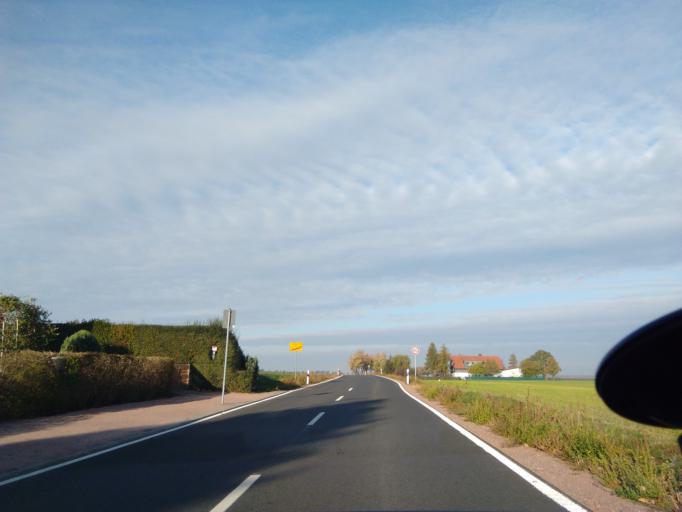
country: DE
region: Saxony
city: Meissen
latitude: 51.1805
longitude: 13.4888
